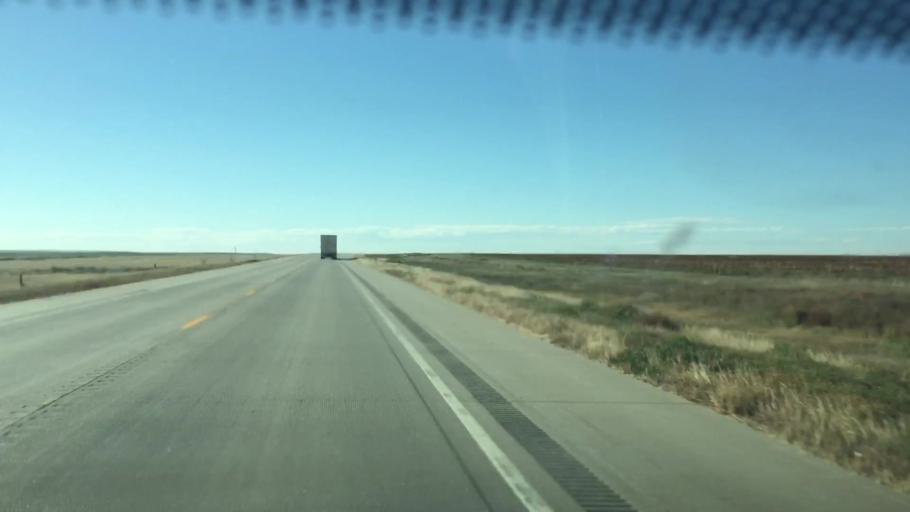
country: US
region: Colorado
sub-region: Kiowa County
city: Eads
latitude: 38.7879
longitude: -102.9266
